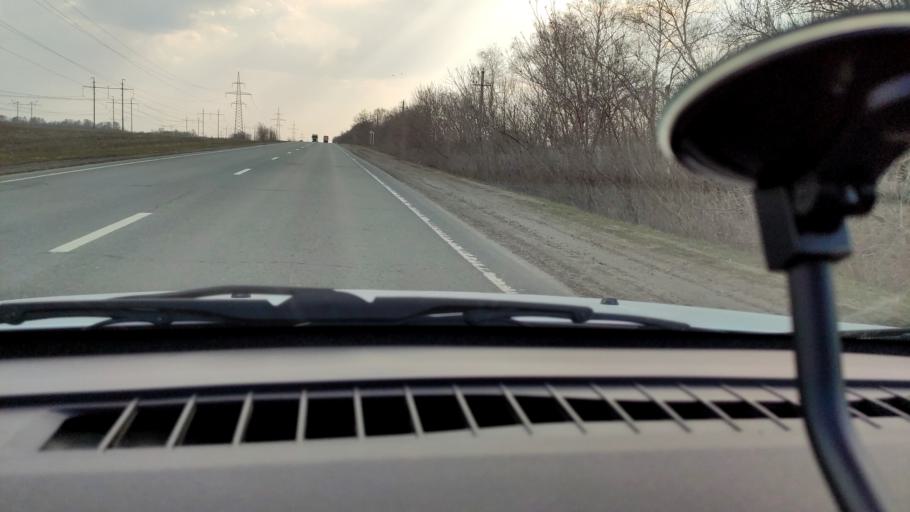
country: RU
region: Samara
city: Dubovyy Umet
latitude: 53.0799
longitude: 50.3895
